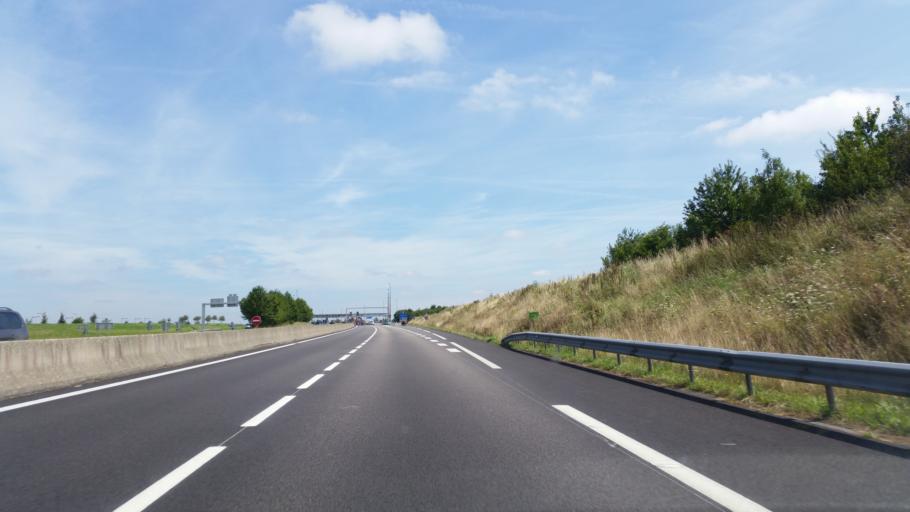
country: FR
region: Haute-Normandie
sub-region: Departement de la Seine-Maritime
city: Aumale
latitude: 49.7560
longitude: 1.6964
